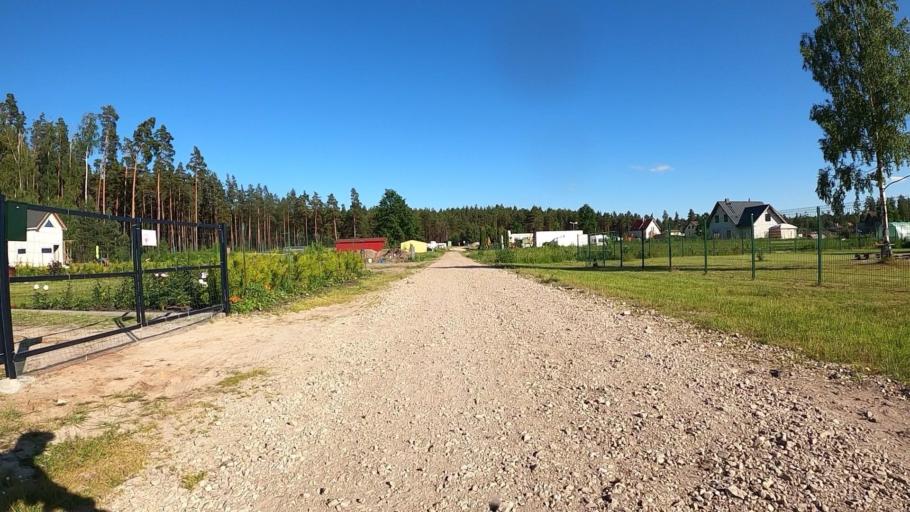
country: LV
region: Stopini
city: Ulbroka
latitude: 56.8831
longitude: 24.2974
